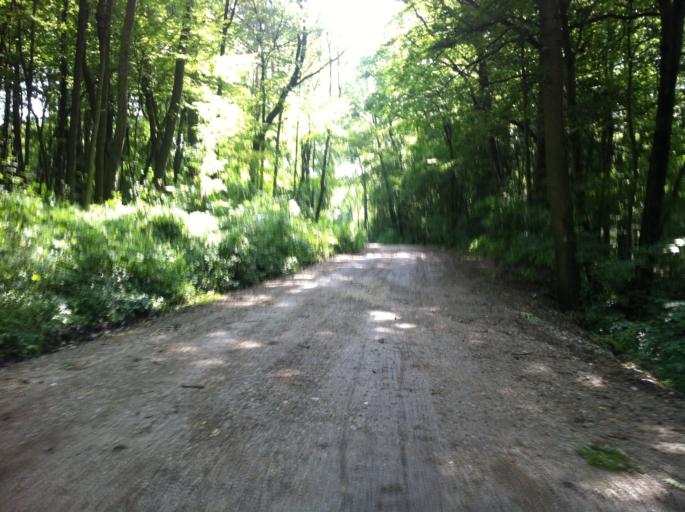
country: AT
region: Lower Austria
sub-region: Politischer Bezirk Modling
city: Laab im Walde
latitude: 48.1801
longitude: 16.1676
